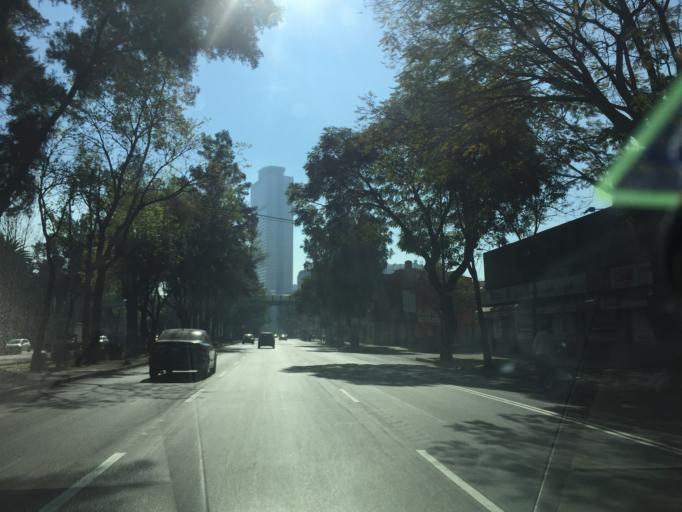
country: MX
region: Mexico City
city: Miguel Hidalgo
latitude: 19.4445
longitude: -99.1794
